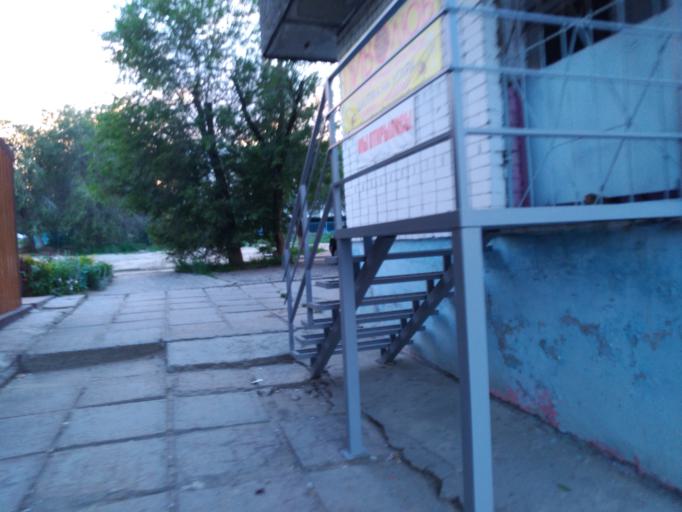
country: RU
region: Volgograd
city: Volgograd
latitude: 48.6718
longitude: 44.4503
